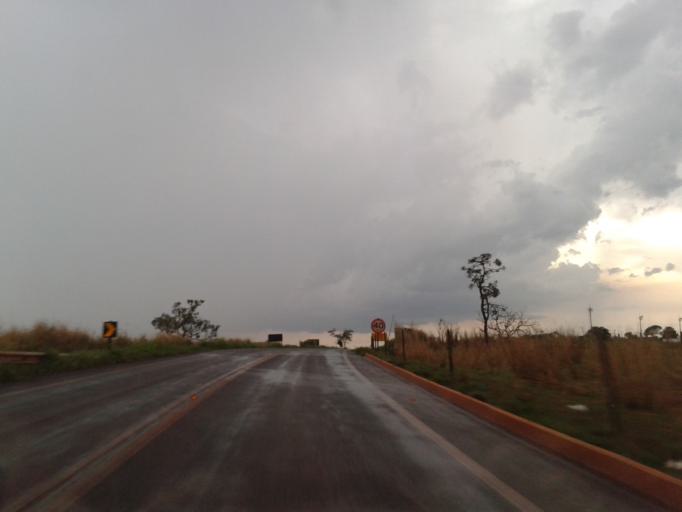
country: BR
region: Goias
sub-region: Quirinopolis
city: Quirinopolis
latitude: -18.4444
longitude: -50.4165
